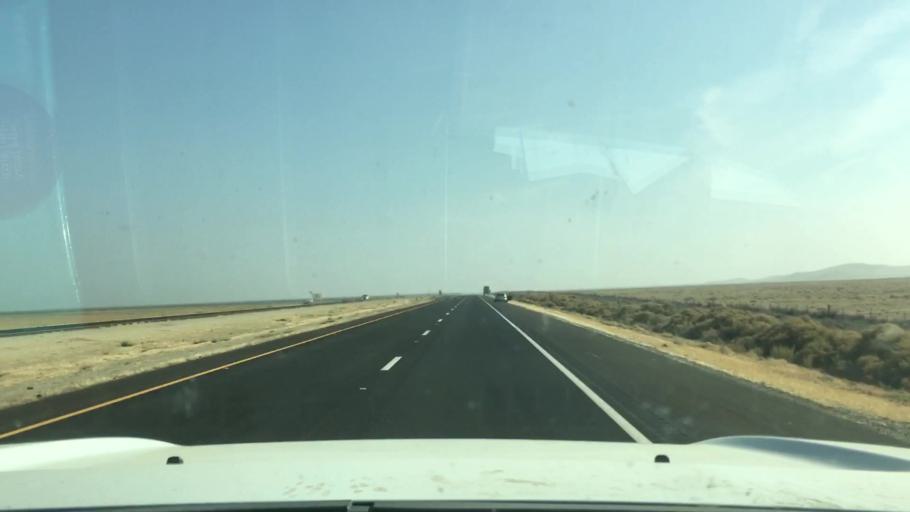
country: US
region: California
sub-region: Kern County
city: Lost Hills
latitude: 35.6338
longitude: -120.0053
